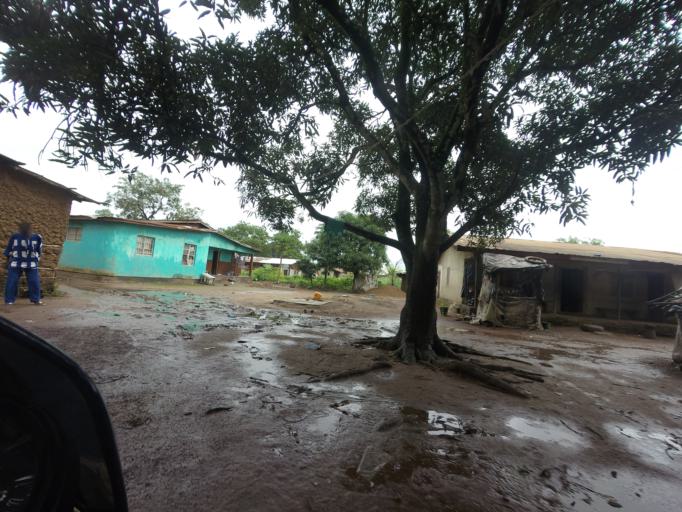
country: SL
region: Northern Province
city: Kambia
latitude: 9.1077
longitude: -12.9234
